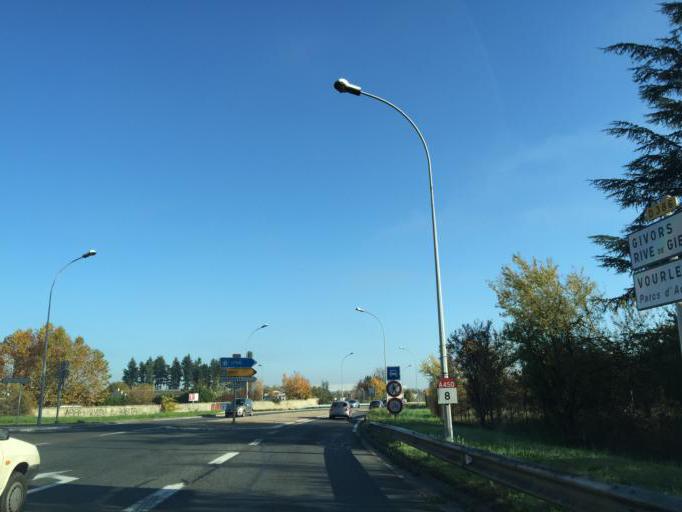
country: FR
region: Rhone-Alpes
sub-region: Departement du Rhone
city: Brignais
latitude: 45.6597
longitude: 4.7519
